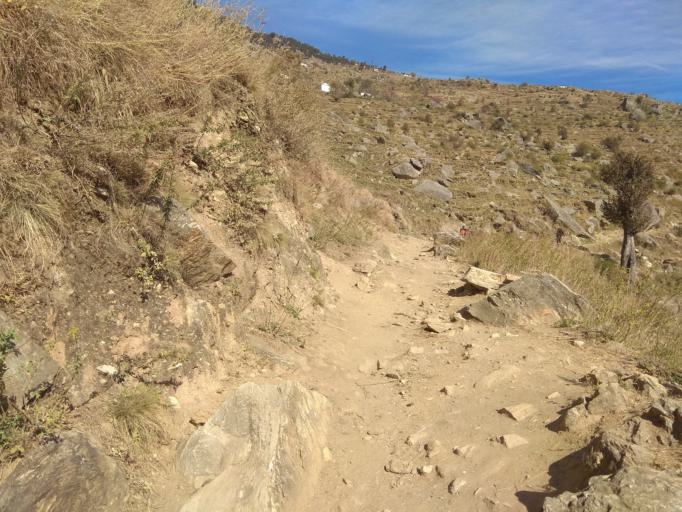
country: NP
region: Mid Western
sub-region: Bheri Zone
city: Dailekh
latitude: 29.2954
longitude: 81.7158
